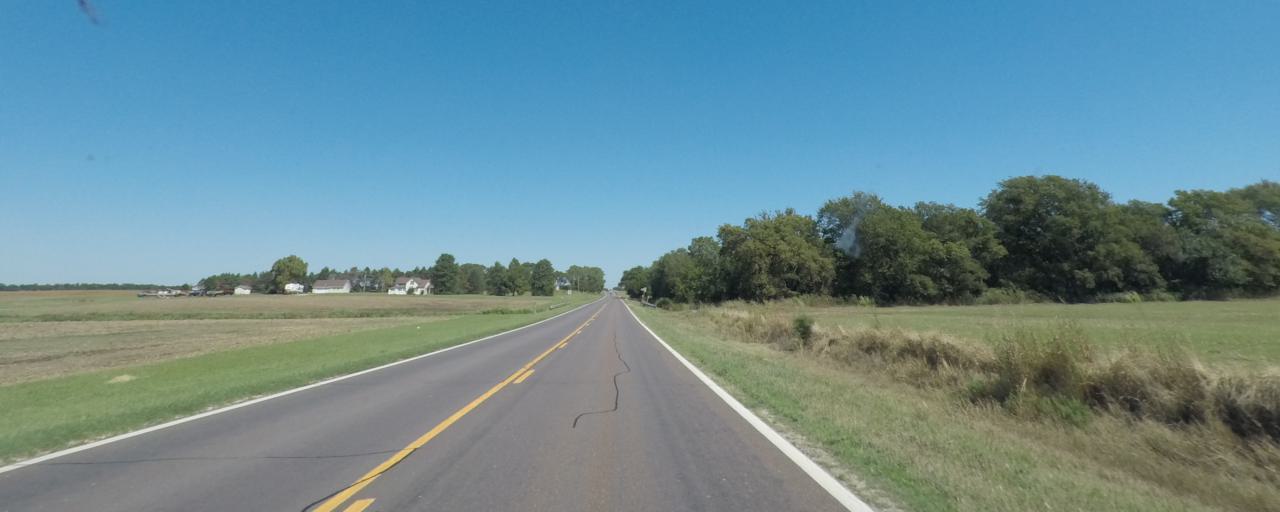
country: US
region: Kansas
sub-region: Sumner County
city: Wellington
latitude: 37.1259
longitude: -97.4016
